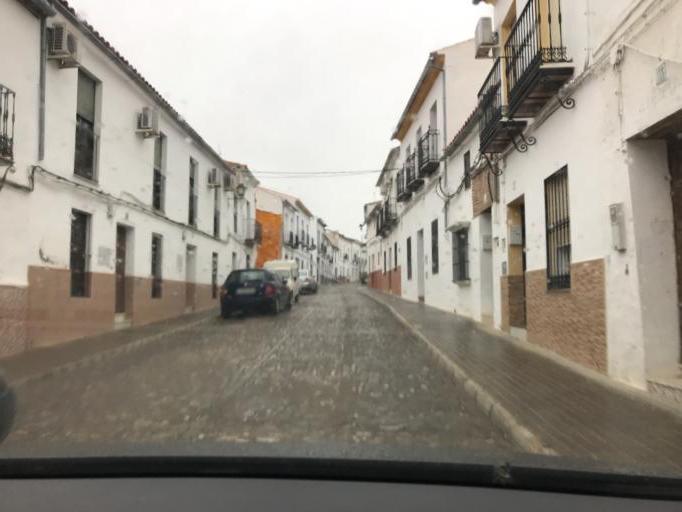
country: ES
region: Andalusia
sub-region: Provincia de Sevilla
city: Guadalcanal
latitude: 38.0914
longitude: -5.8223
